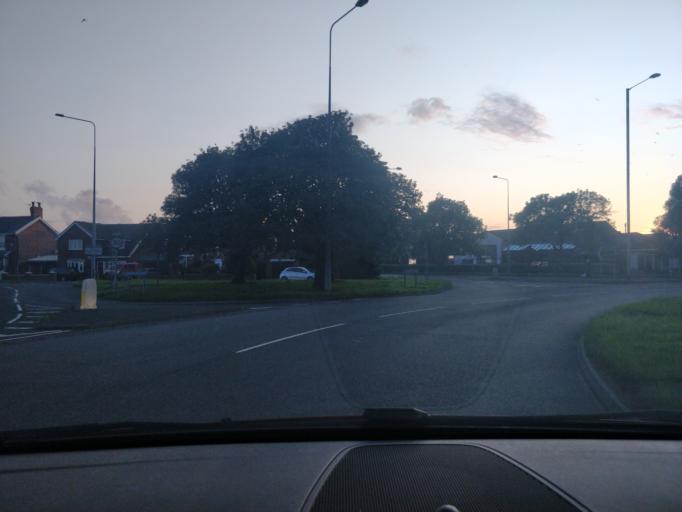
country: GB
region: England
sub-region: Lancashire
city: Tarleton
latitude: 53.7069
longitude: -2.7946
